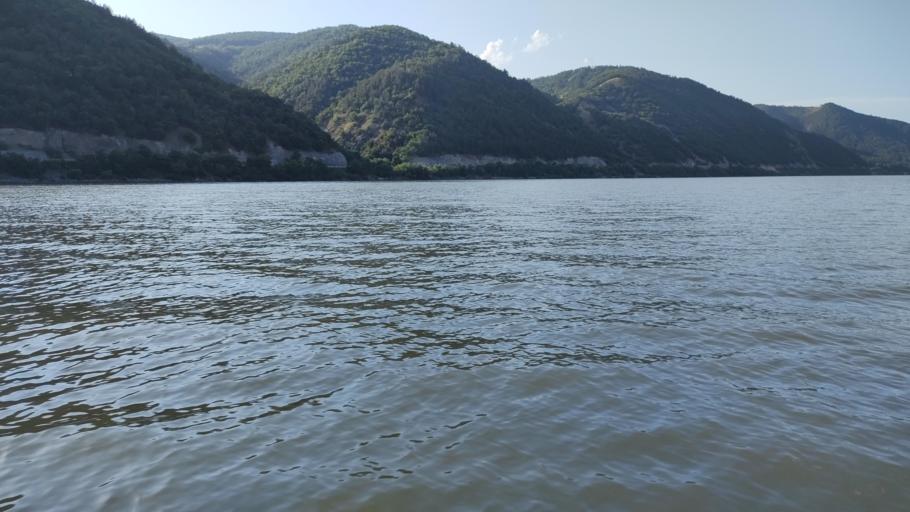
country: RO
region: Mehedinti
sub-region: Comuna Svinita
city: Svinita
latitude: 44.4978
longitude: 22.1902
